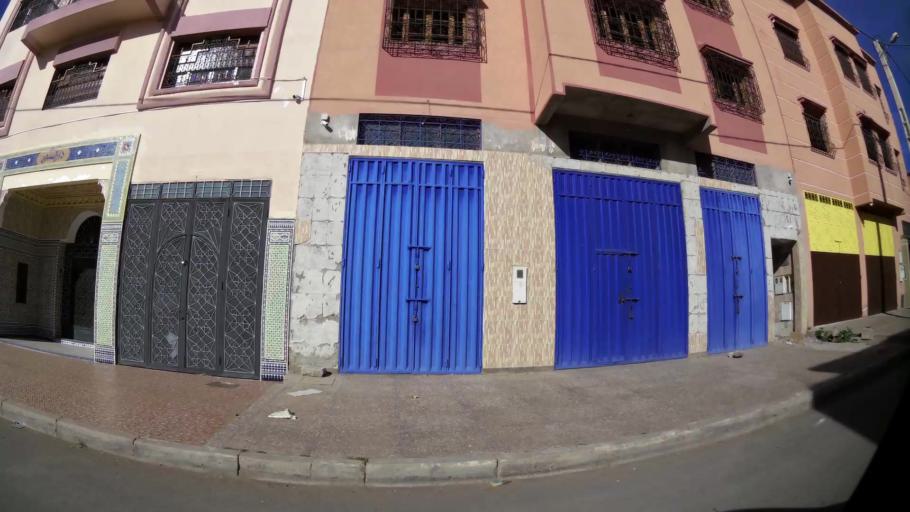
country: MA
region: Marrakech-Tensift-Al Haouz
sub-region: Marrakech
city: Marrakesh
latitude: 31.6791
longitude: -8.0421
